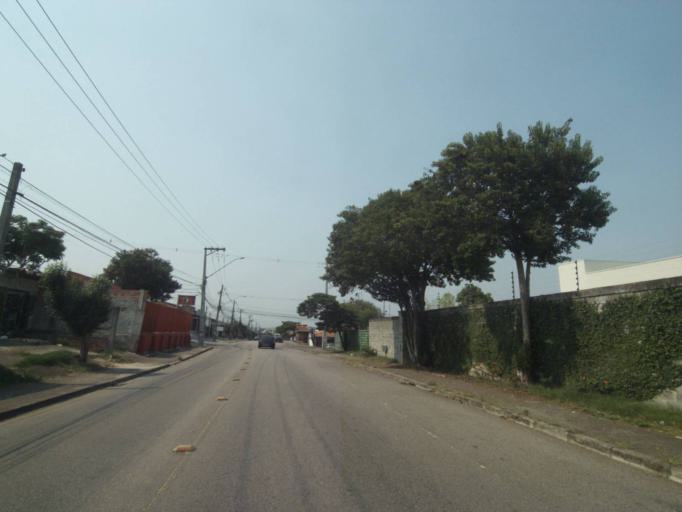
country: BR
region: Parana
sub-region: Sao Jose Dos Pinhais
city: Sao Jose dos Pinhais
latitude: -25.5204
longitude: -49.2482
